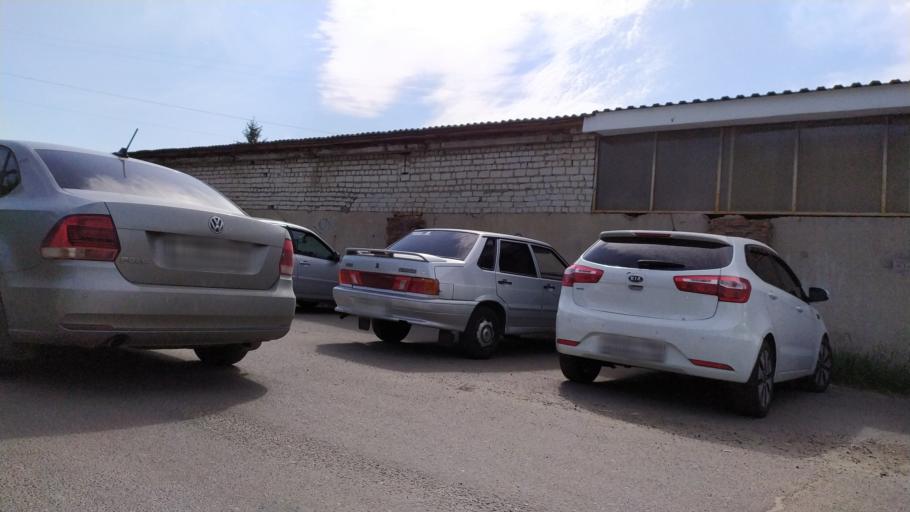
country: RU
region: Kursk
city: Kursk
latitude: 51.6648
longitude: 36.1510
